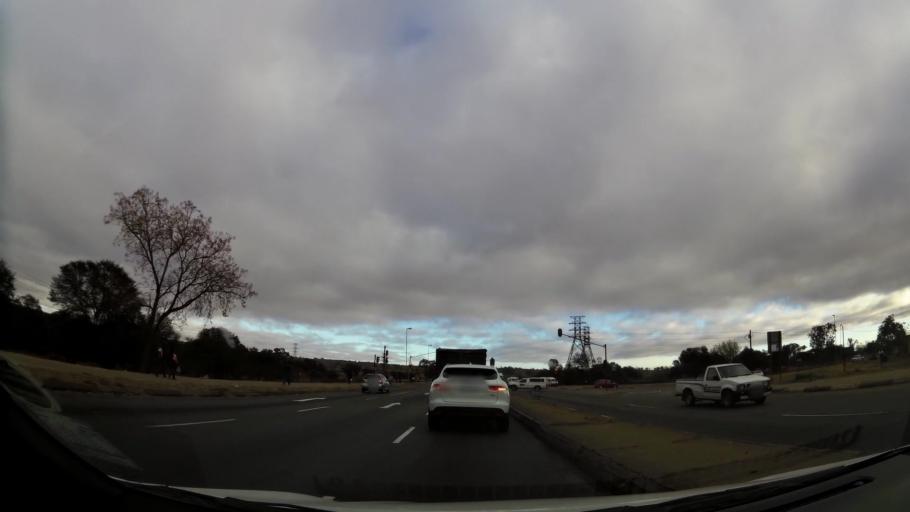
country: ZA
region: Limpopo
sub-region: Capricorn District Municipality
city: Polokwane
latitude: -23.8879
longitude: 29.4302
